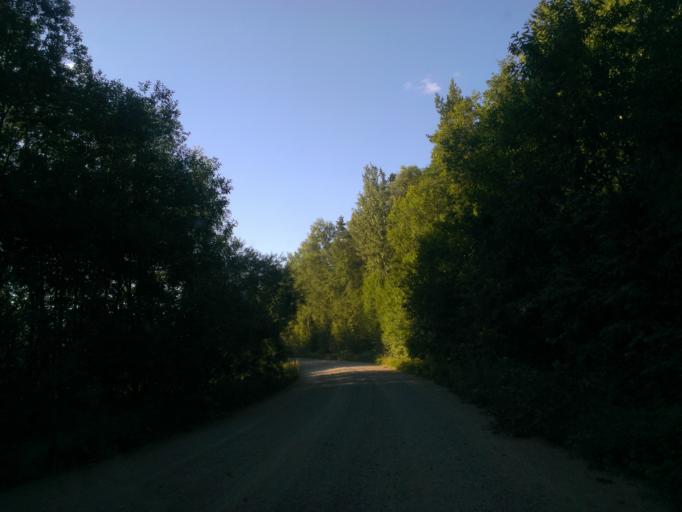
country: LV
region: Malpils
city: Malpils
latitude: 57.0960
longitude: 25.0471
